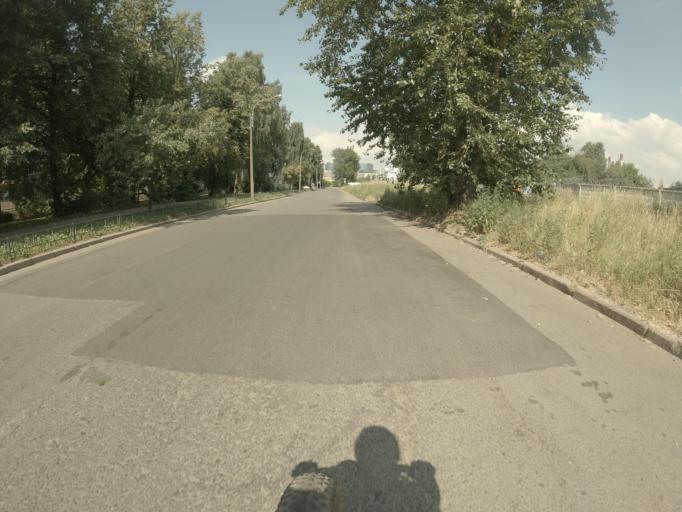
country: RU
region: St.-Petersburg
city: Krasnogvargeisky
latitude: 59.9262
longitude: 30.4305
